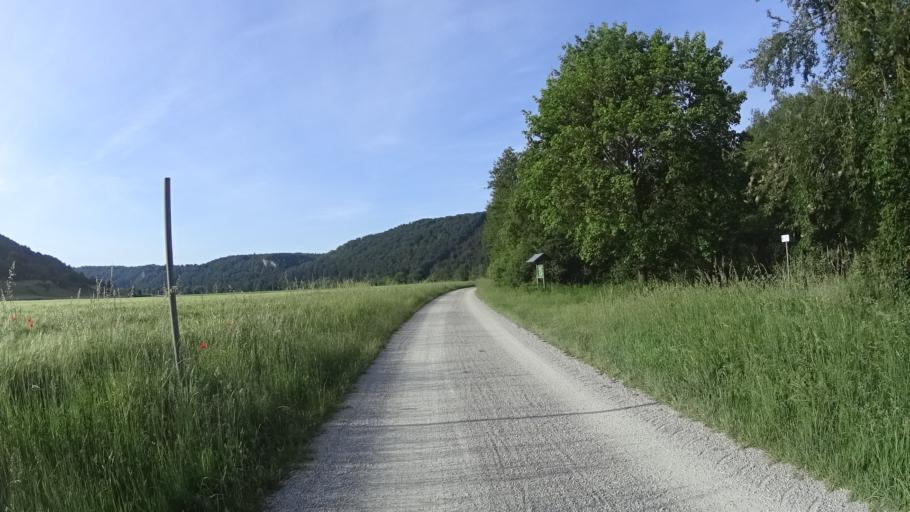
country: DE
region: Bavaria
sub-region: Lower Bavaria
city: Riedenburg
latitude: 48.9884
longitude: 11.6331
